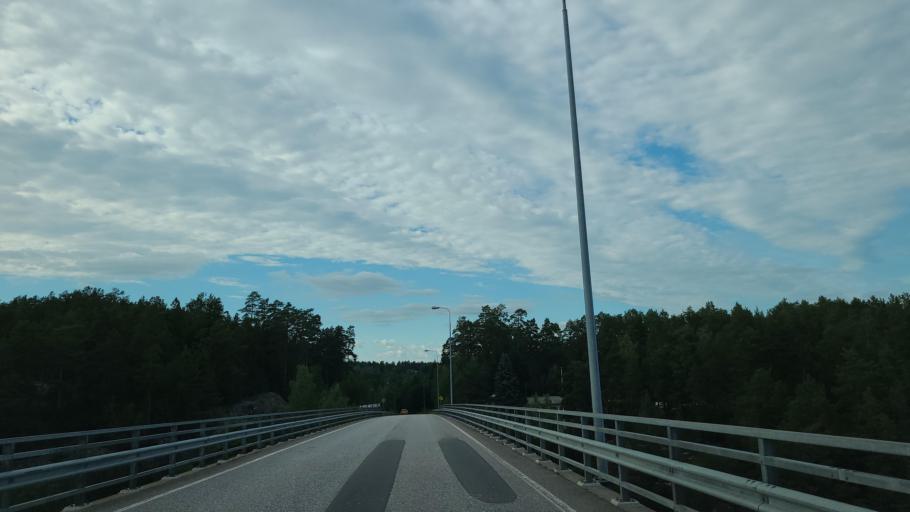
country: FI
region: Varsinais-Suomi
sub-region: Turku
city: Rymaettylae
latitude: 60.3373
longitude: 21.9794
